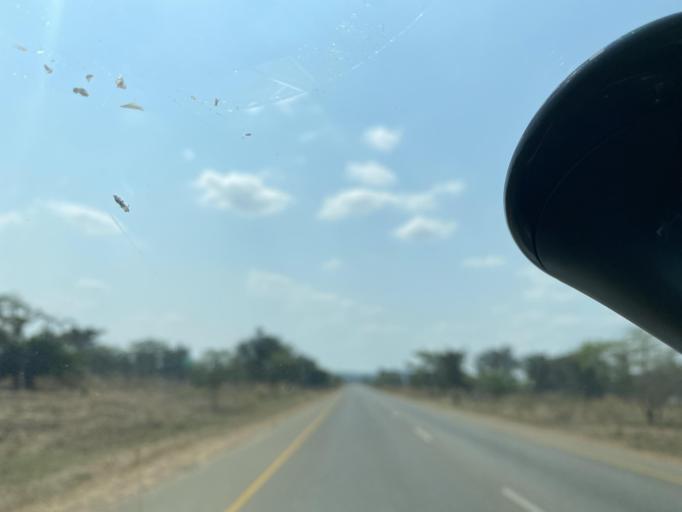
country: ZM
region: Lusaka
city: Chongwe
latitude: -15.5617
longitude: 28.6872
